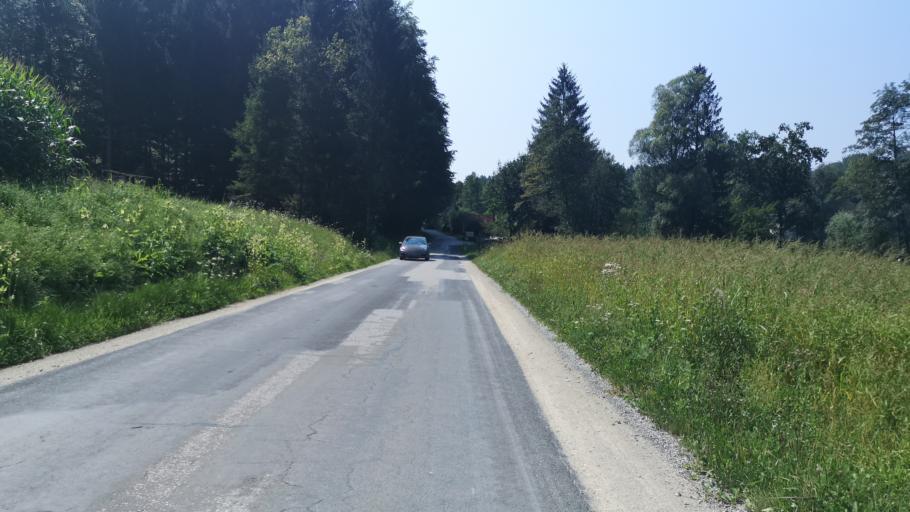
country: AT
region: Styria
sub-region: Politischer Bezirk Deutschlandsberg
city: Sankt Josef (Weststeiermark)
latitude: 46.9011
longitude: 15.3641
